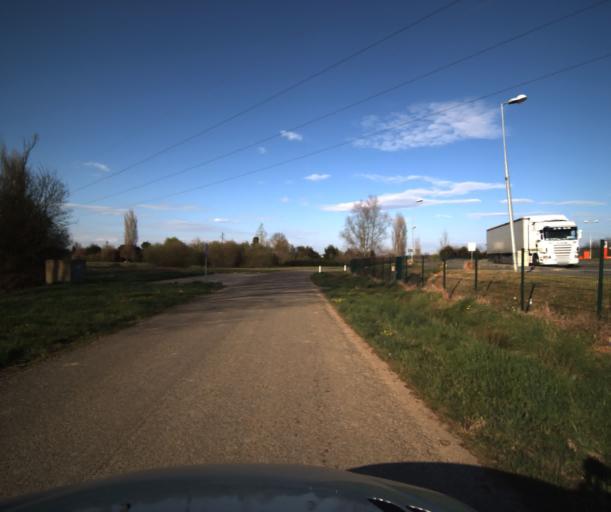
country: FR
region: Midi-Pyrenees
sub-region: Departement du Tarn-et-Garonne
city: Bressols
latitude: 43.9579
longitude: 1.3260
